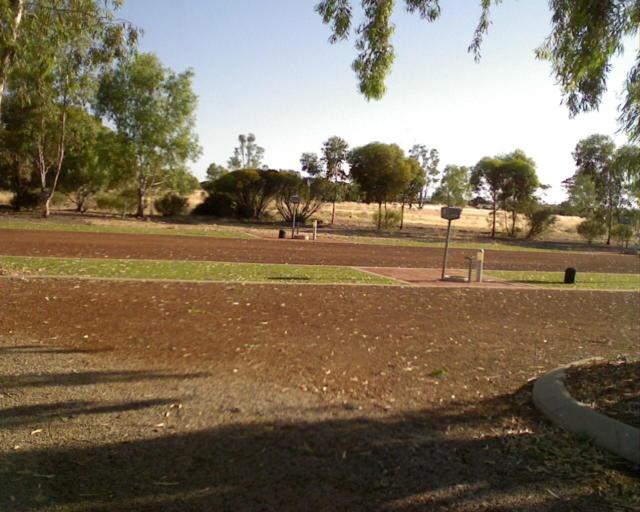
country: AU
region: Western Australia
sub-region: Merredin
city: Merredin
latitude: -31.1114
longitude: 117.7934
